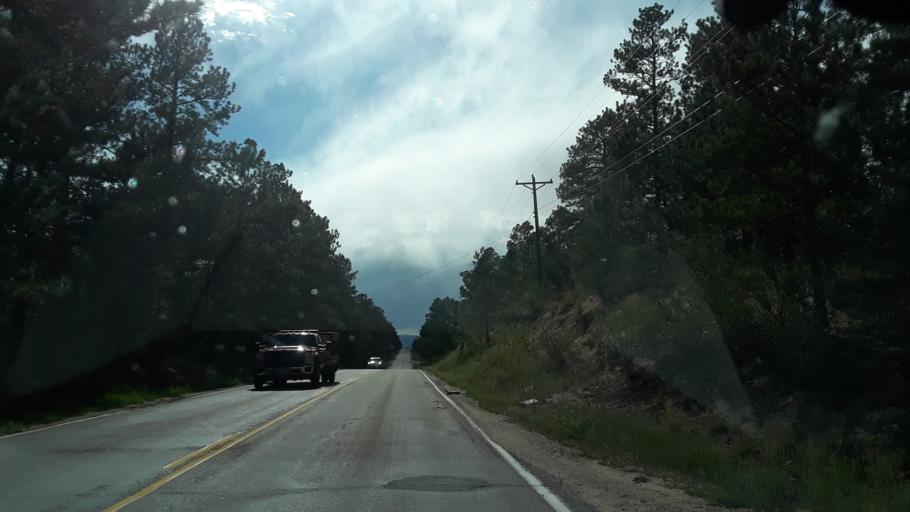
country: US
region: Colorado
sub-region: El Paso County
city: Black Forest
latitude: 39.0128
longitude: -104.7159
